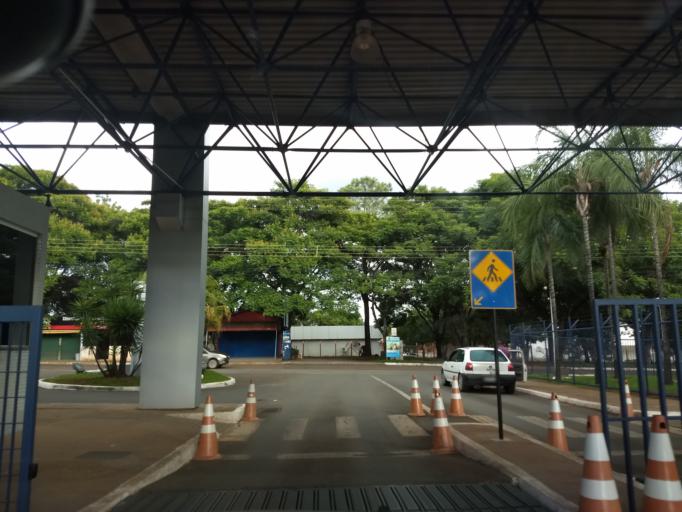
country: BR
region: Federal District
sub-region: Brasilia
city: Brasilia
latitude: -15.8110
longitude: -47.9585
